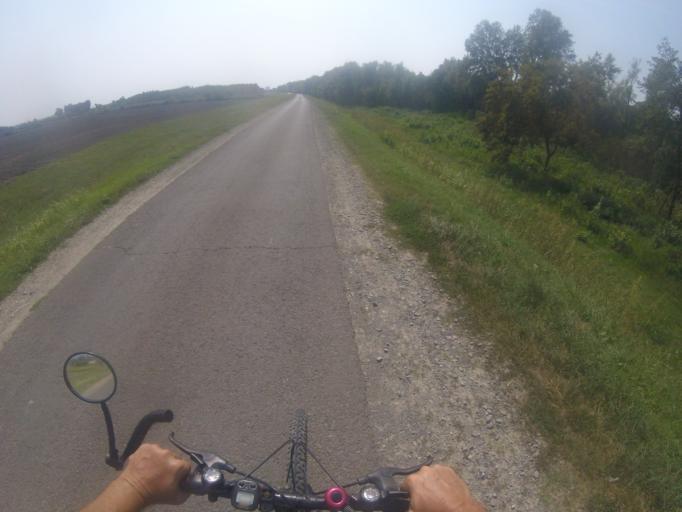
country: HU
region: Bacs-Kiskun
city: Baja
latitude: 46.2157
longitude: 18.9179
